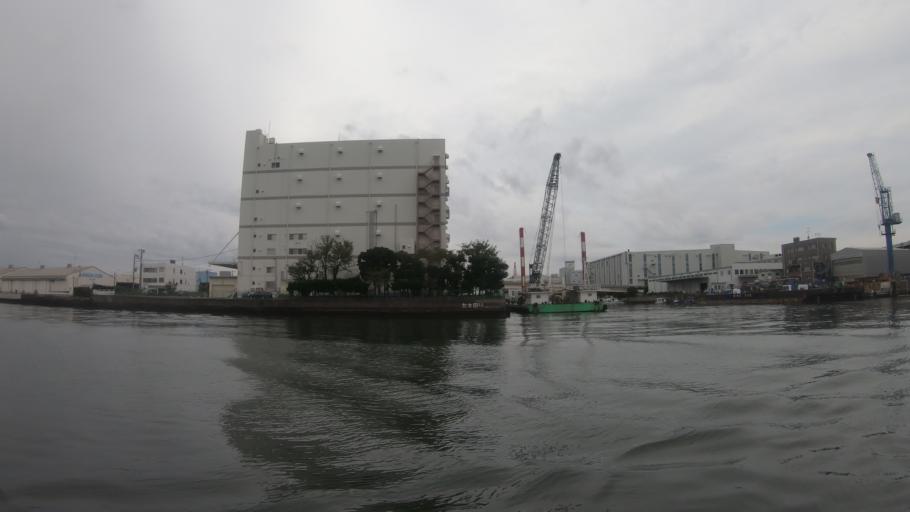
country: JP
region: Kanagawa
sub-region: Kawasaki-shi
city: Kawasaki
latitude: 35.4915
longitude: 139.6778
